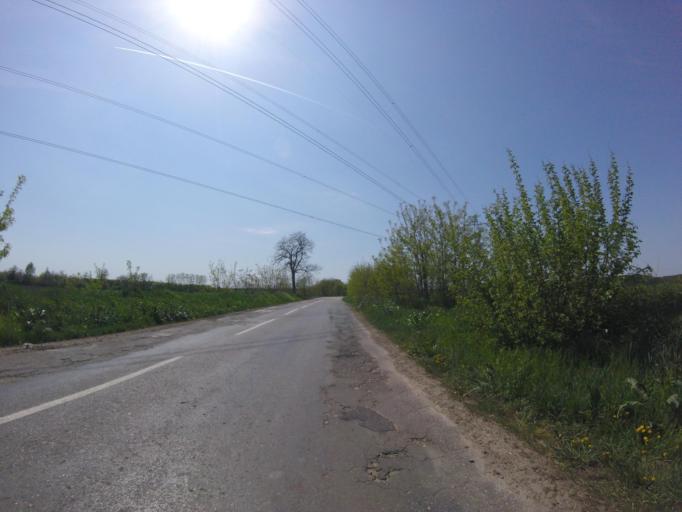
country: HU
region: Pest
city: Nyaregyhaza
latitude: 47.2483
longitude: 19.4859
